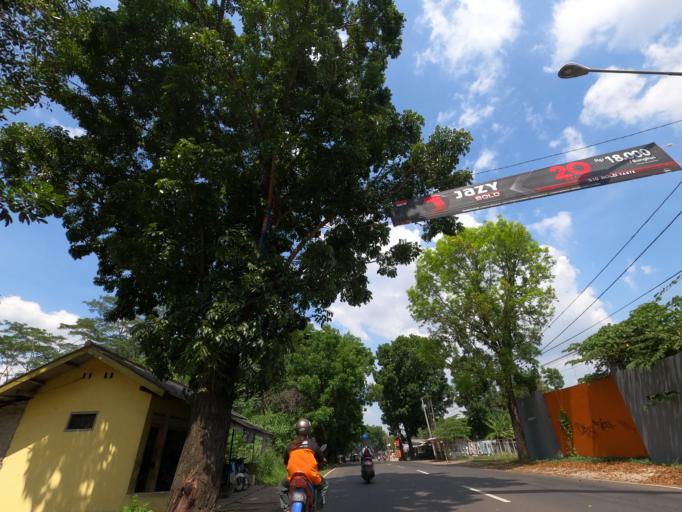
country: ID
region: West Java
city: Pamanukan
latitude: -6.5534
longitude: 107.7478
